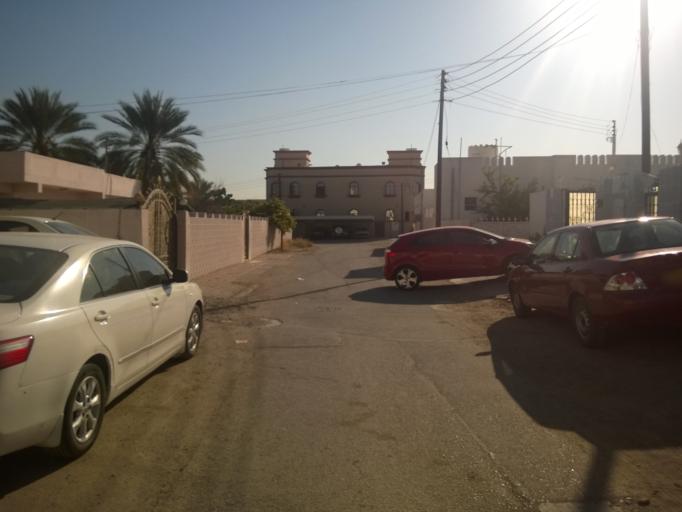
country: OM
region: Muhafazat Masqat
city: As Sib al Jadidah
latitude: 23.6664
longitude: 58.1873
